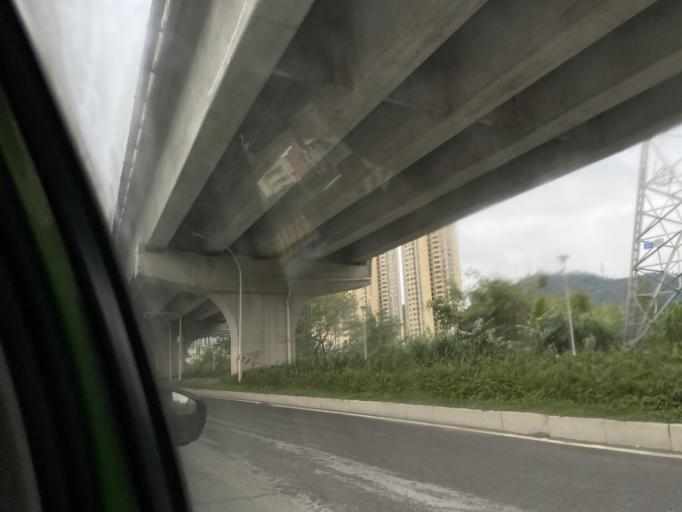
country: CN
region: Guangdong
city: Nanping
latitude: 22.1765
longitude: 113.4775
